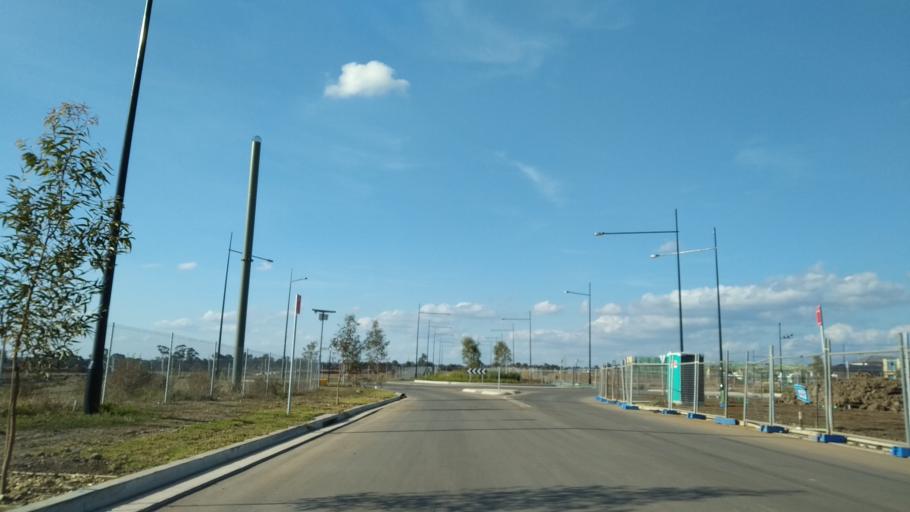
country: AU
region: New South Wales
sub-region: Blacktown
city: Blackett
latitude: -33.6896
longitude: 150.8136
